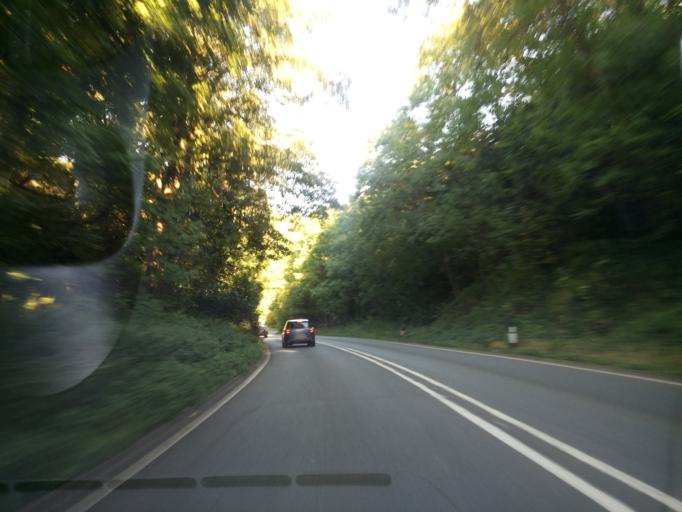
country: GB
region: England
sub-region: Derbyshire
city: Tideswell
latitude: 53.2387
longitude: -1.7685
